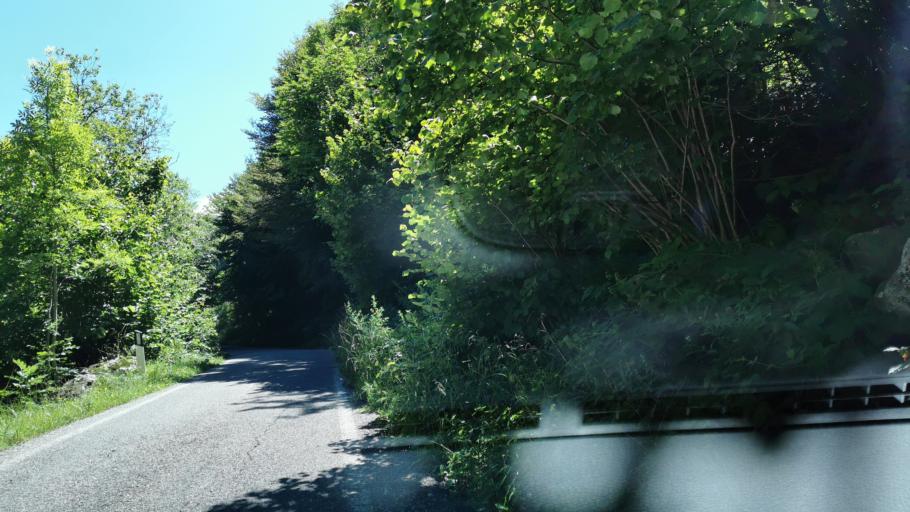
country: IT
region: Piedmont
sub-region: Provincia di Cuneo
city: Entracque
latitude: 44.1907
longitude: 7.3836
